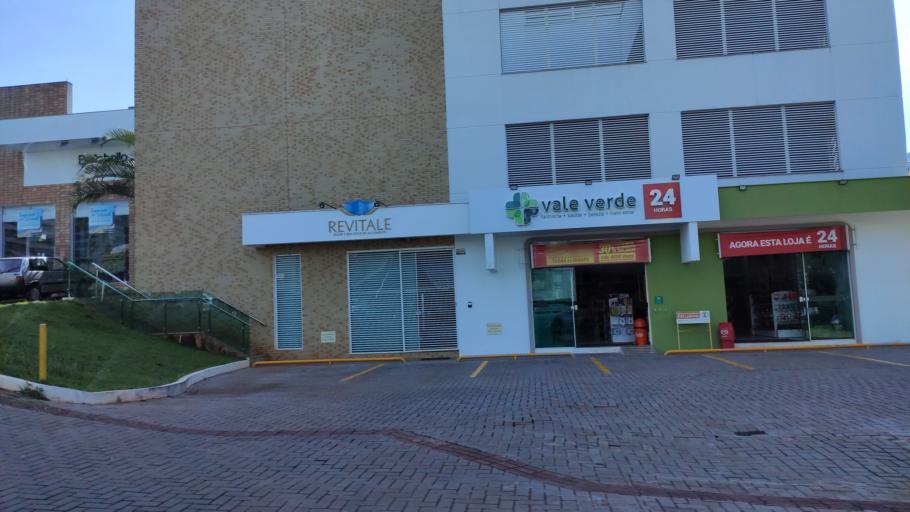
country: BR
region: Parana
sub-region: Londrina
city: Londrina
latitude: -23.3342
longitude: -51.1777
